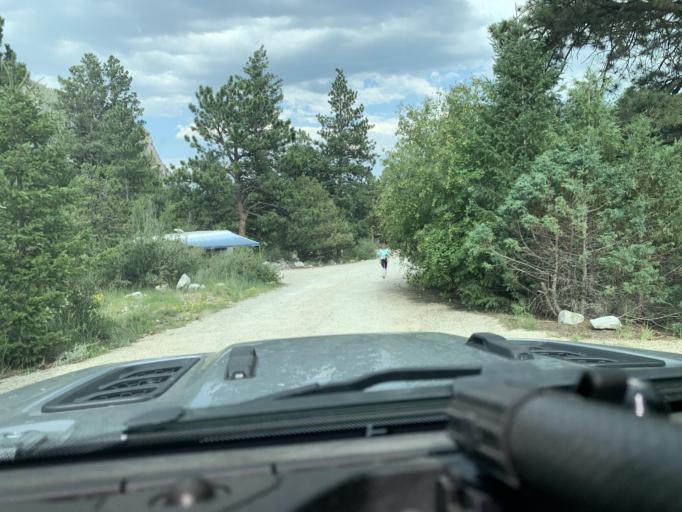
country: US
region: Colorado
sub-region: Chaffee County
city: Buena Vista
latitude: 38.7136
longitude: -106.2239
